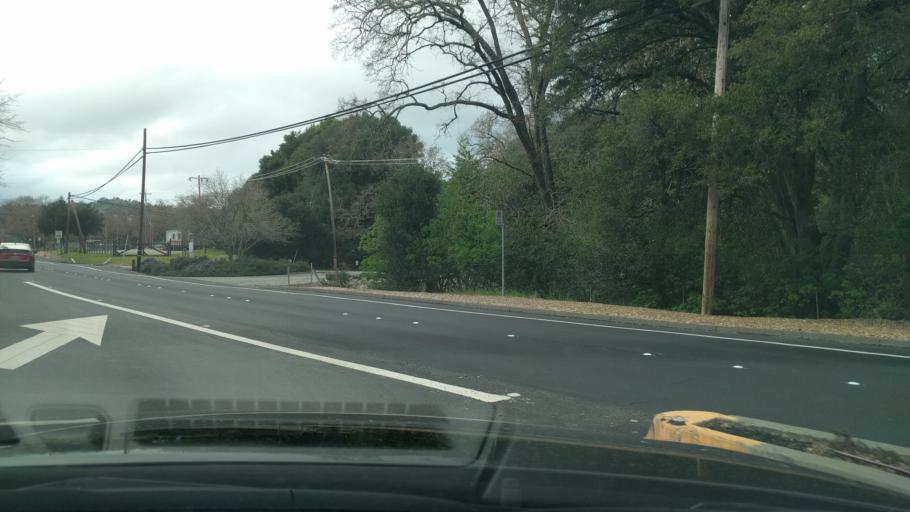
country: US
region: California
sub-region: Contra Costa County
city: Lafayette
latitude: 37.8882
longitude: -122.1399
